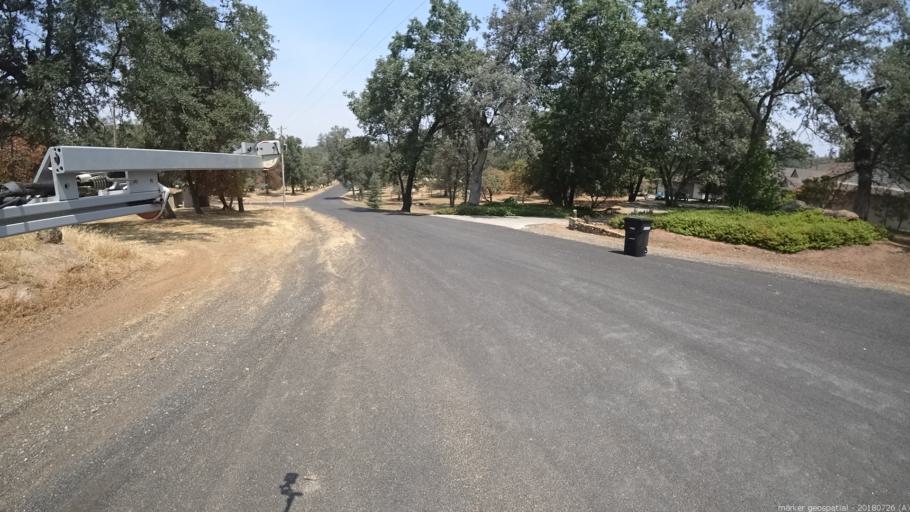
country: US
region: California
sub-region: Madera County
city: Oakhurst
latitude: 37.2815
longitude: -119.6371
